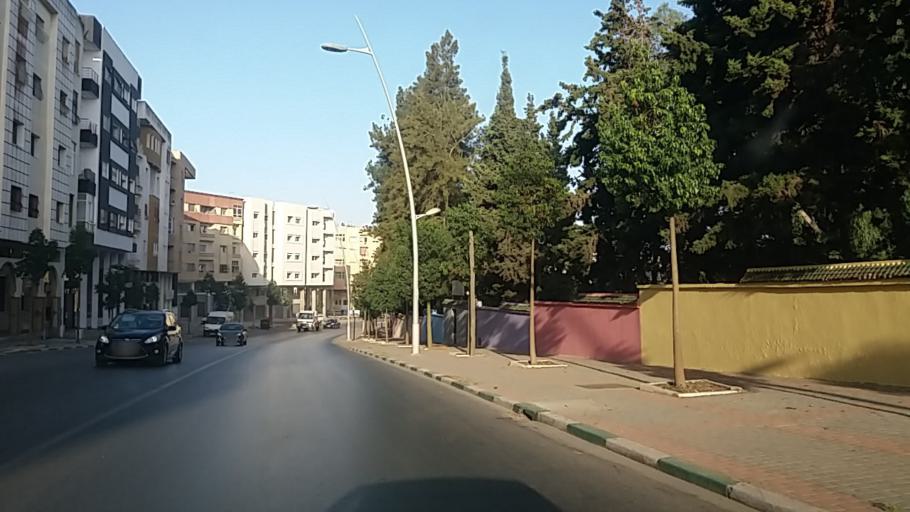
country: MA
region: Gharb-Chrarda-Beni Hssen
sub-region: Kenitra Province
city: Kenitra
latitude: 34.2560
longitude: -6.6072
